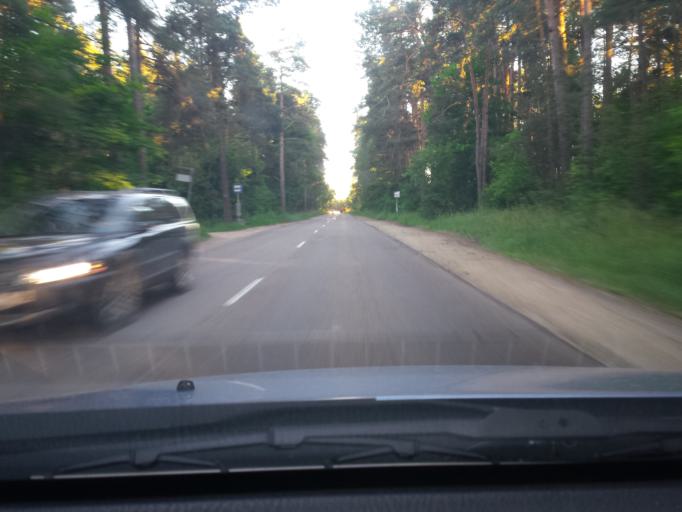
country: LV
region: Riga
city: Jaunciems
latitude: 57.0324
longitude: 24.1875
